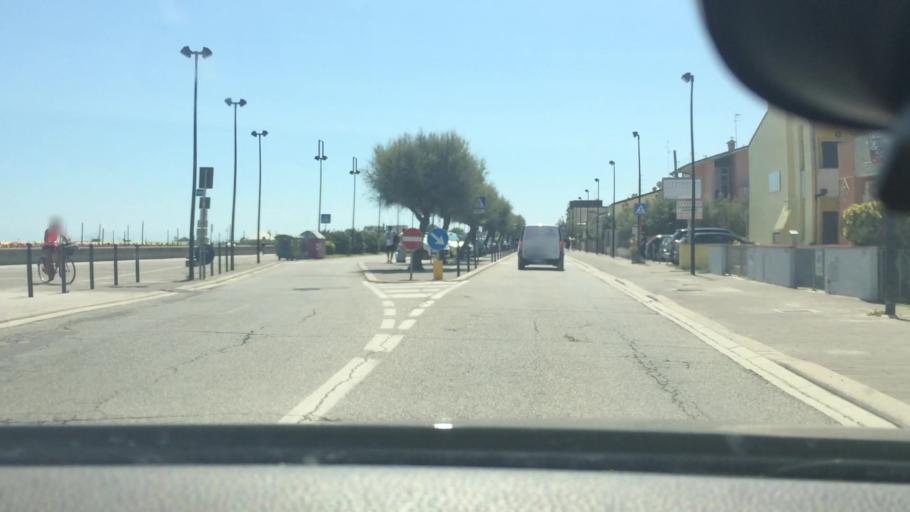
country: IT
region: Emilia-Romagna
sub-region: Provincia di Ferrara
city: Porto Garibaldi
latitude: 44.6859
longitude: 12.2403
